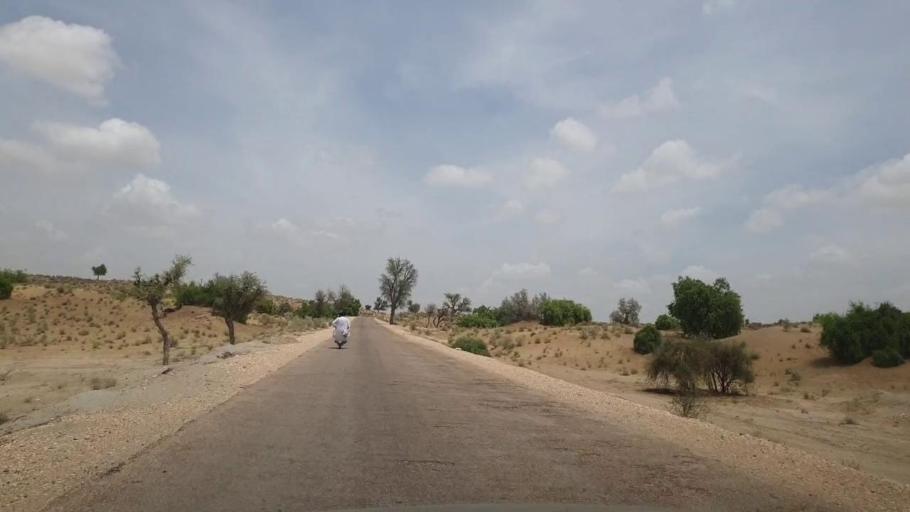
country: PK
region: Sindh
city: Kot Diji
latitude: 27.1810
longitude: 69.1789
